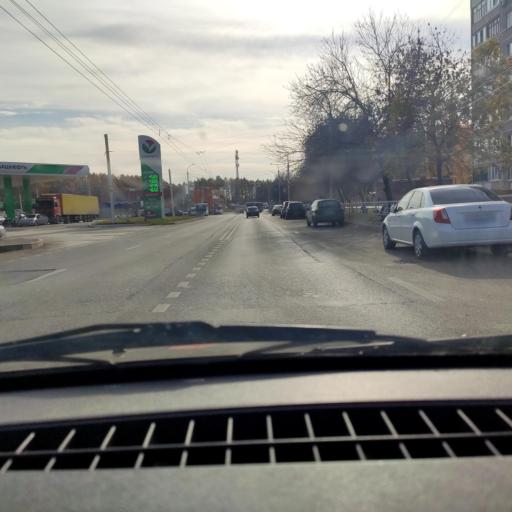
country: RU
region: Bashkortostan
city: Ufa
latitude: 54.6989
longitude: 56.0067
